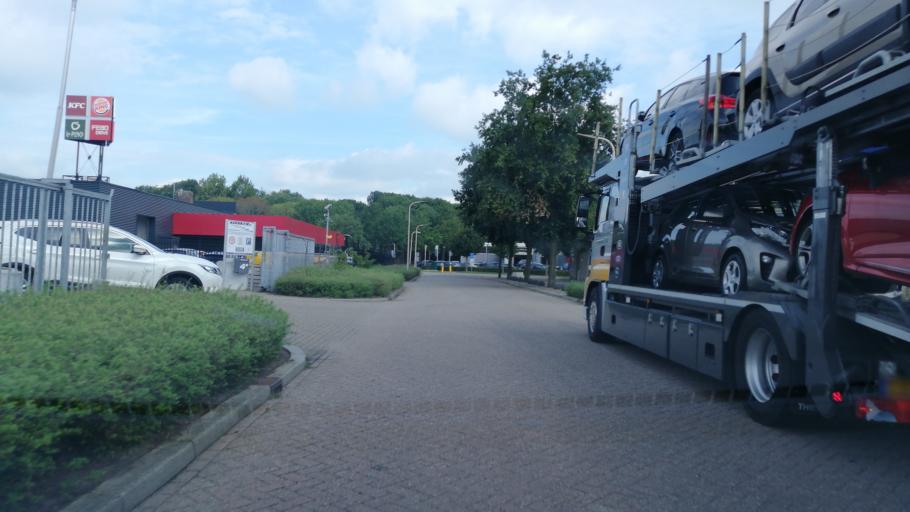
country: NL
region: Overijssel
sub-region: Gemeente Zwolle
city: Zwolle
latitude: 52.5237
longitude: 6.1214
